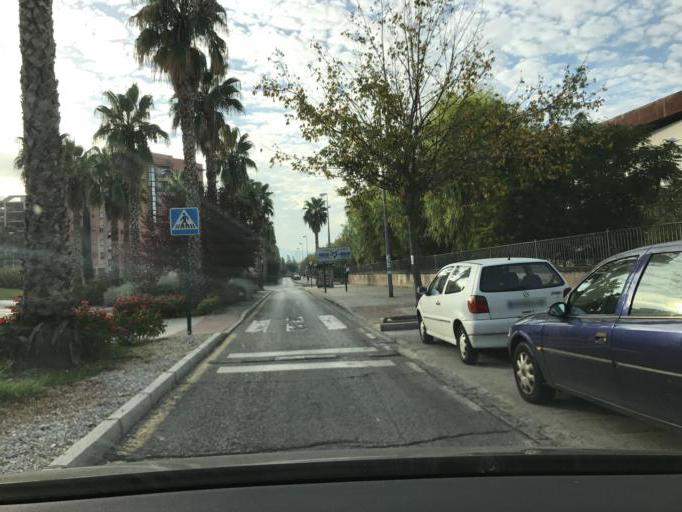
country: ES
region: Andalusia
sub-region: Provincia de Granada
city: Maracena
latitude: 37.1967
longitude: -3.6256
